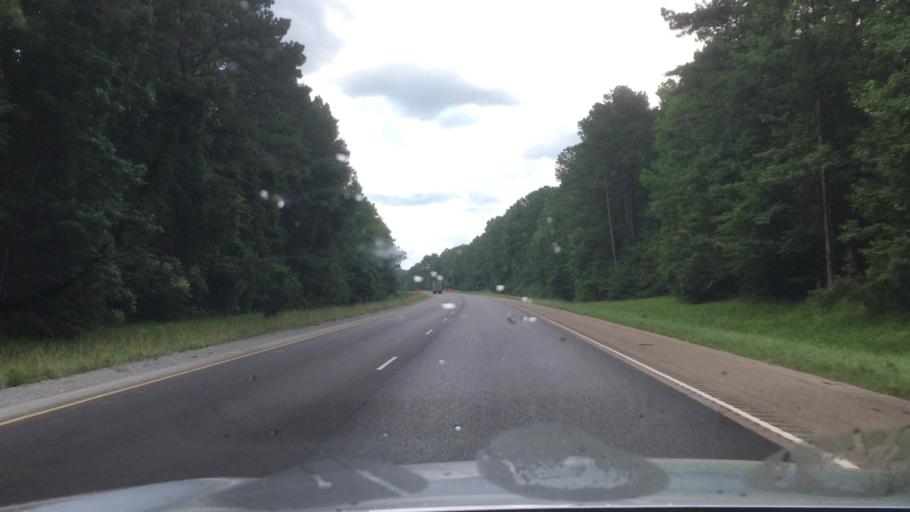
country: US
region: Mississippi
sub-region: Clarke County
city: Stonewall
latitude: 31.9770
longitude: -88.9538
